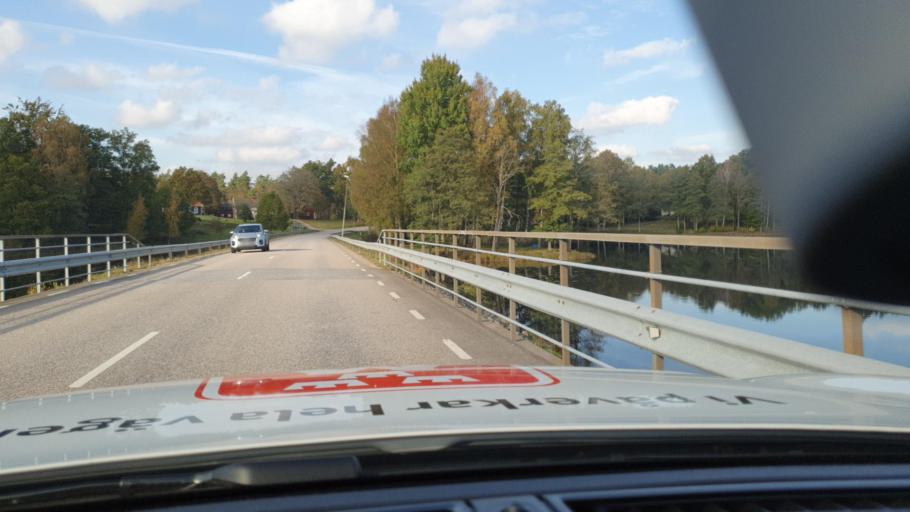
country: SE
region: Kronoberg
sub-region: Markaryds Kommun
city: Markaryd
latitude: 56.4896
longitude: 13.5275
